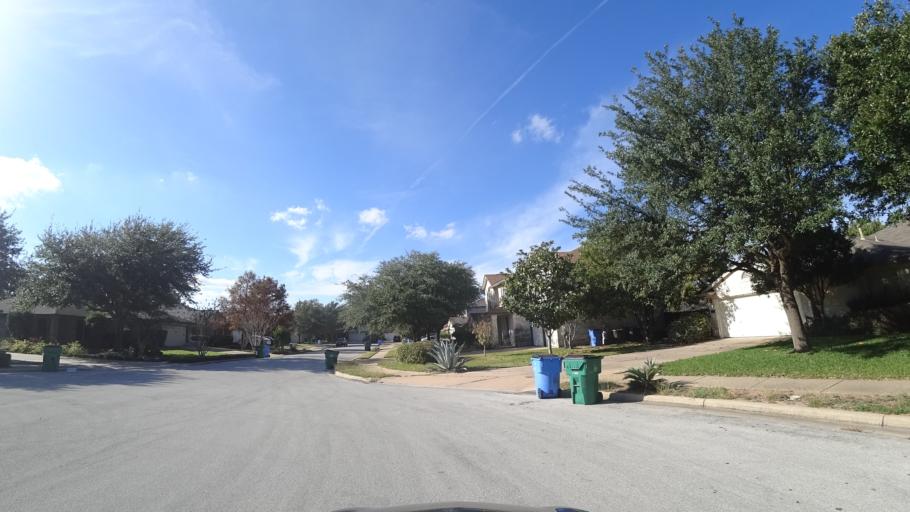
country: US
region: Texas
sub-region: Travis County
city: Wells Branch
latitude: 30.4643
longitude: -97.6858
